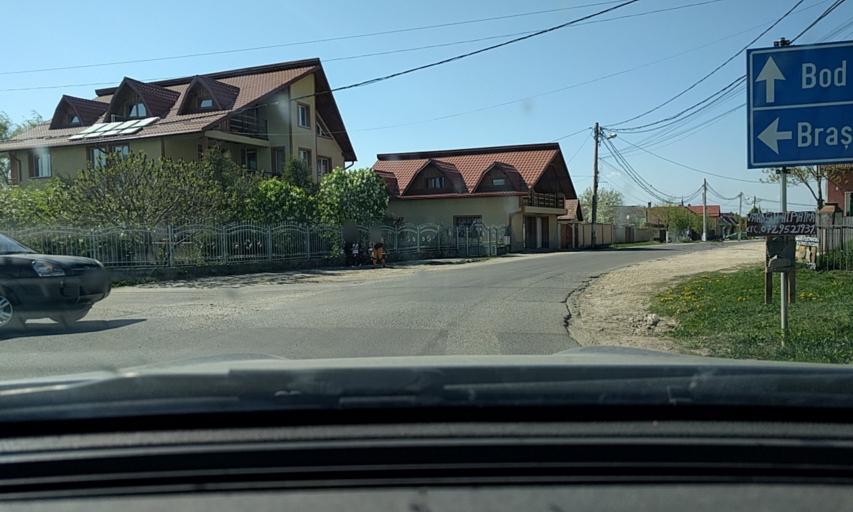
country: RO
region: Brasov
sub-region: Comuna Sanpetru
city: Sanpetru
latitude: 45.7048
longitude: 25.6405
